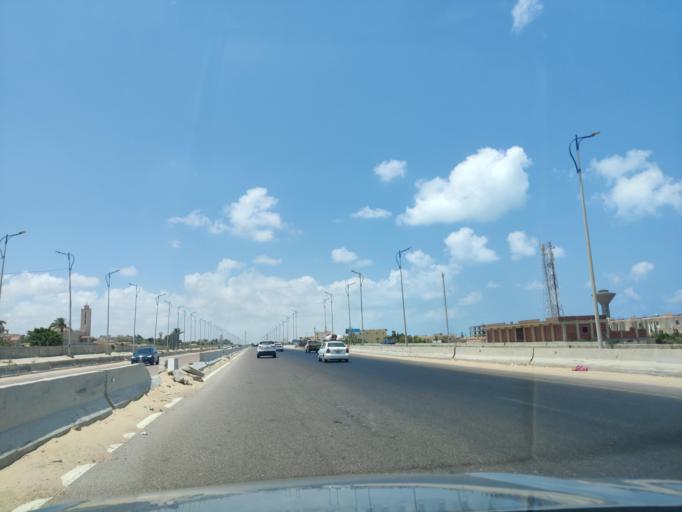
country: EG
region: Alexandria
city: Alexandria
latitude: 30.9742
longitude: 29.5687
